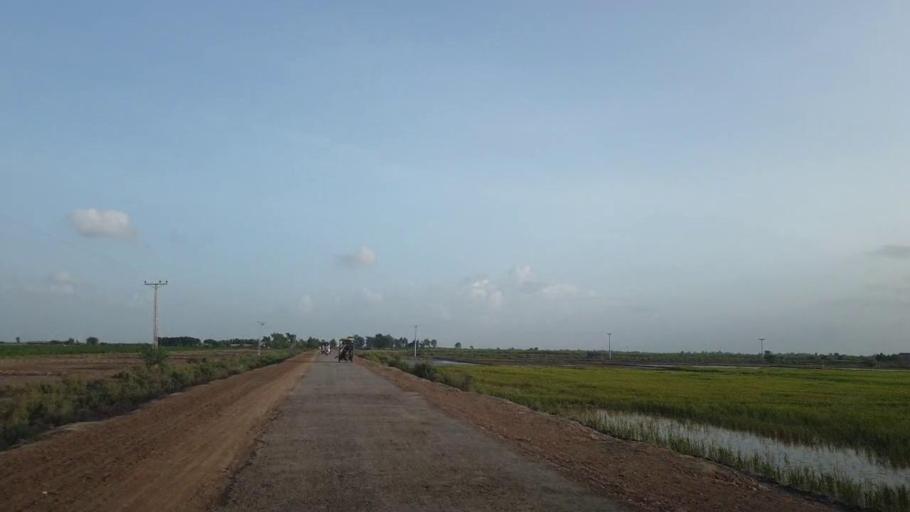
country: PK
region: Sindh
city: Kadhan
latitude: 24.6215
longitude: 69.1158
